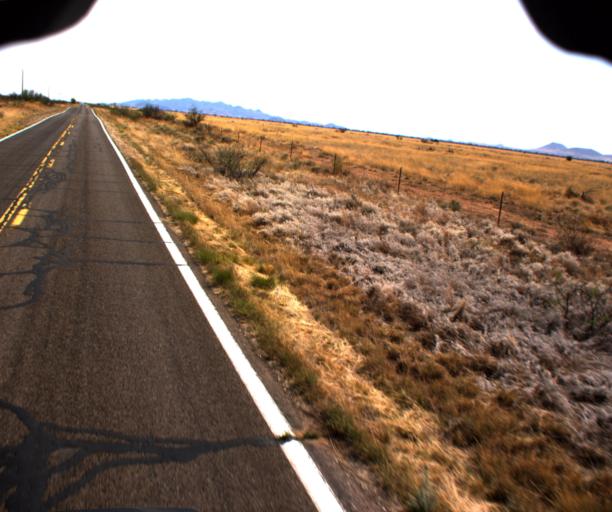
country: US
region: Arizona
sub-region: Cochise County
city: Willcox
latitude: 31.9180
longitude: -109.4915
